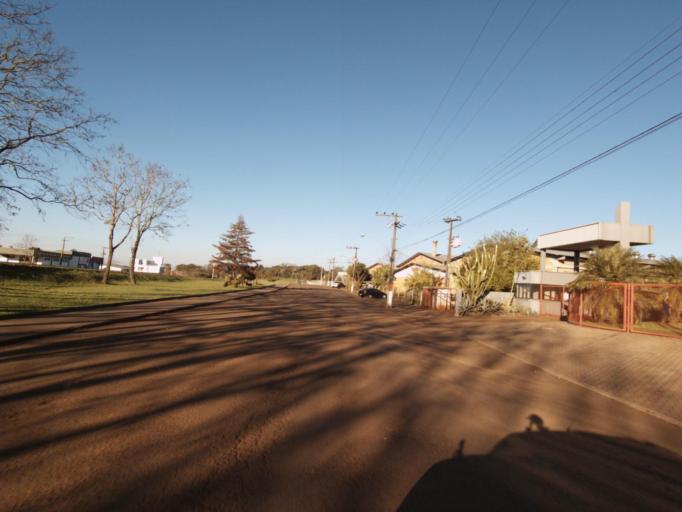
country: BR
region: Santa Catarina
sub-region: Chapeco
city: Chapeco
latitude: -26.9057
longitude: -52.9019
